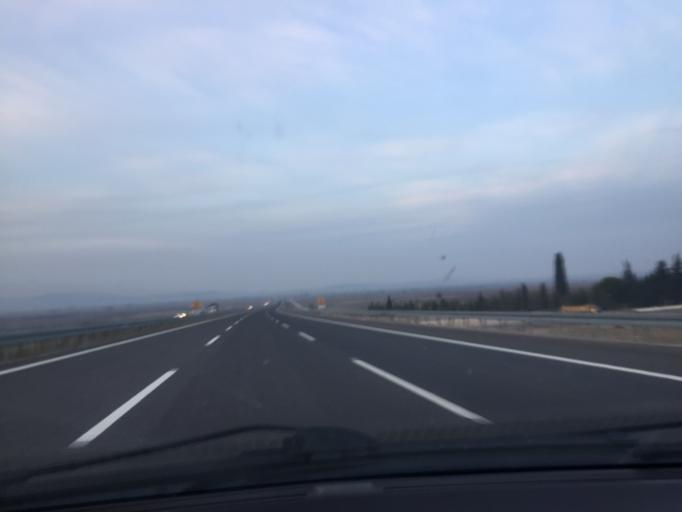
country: TR
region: Manisa
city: Halitpasa
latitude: 38.7031
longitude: 27.6442
